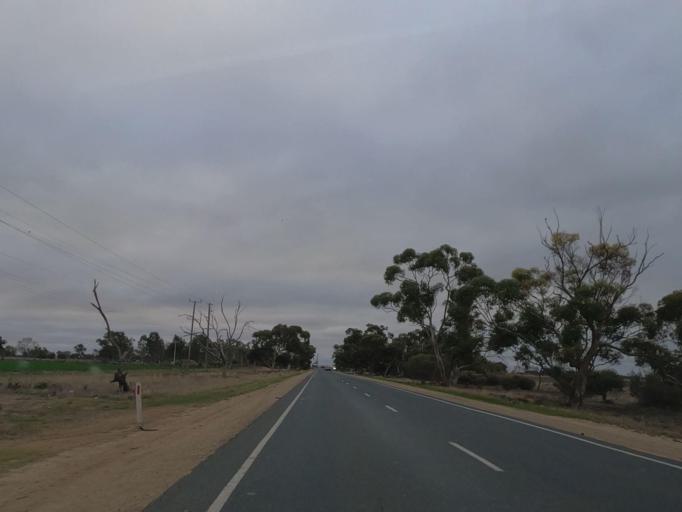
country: AU
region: Victoria
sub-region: Swan Hill
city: Swan Hill
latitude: -35.3989
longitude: 143.5757
